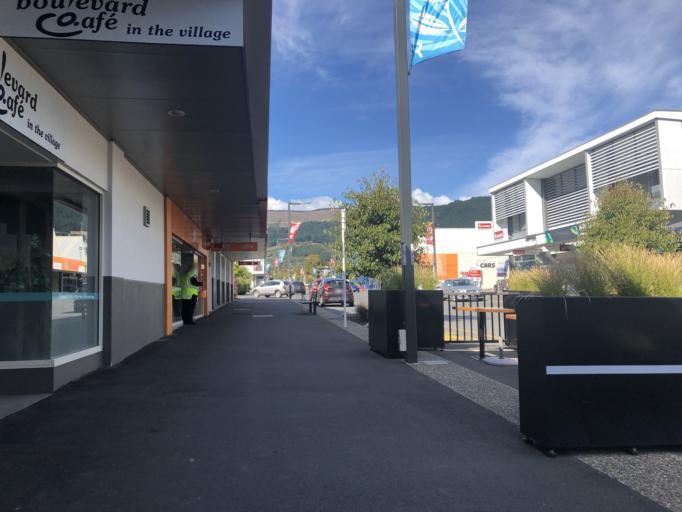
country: NZ
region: Tasman
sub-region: Tasman District
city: Richmond
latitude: -41.3402
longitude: 173.1858
